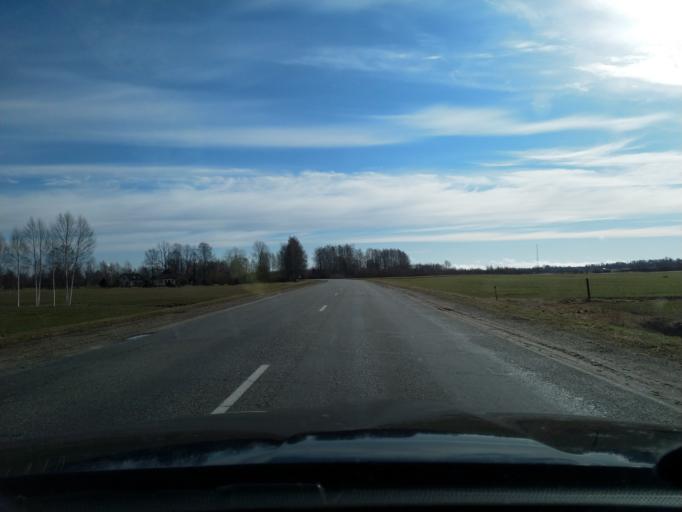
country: LV
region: Kuldigas Rajons
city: Kuldiga
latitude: 56.9552
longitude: 21.9586
